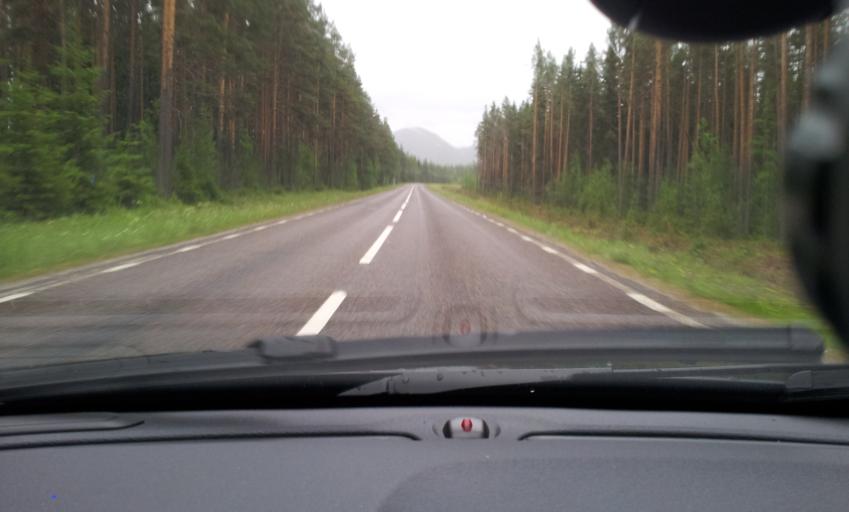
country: SE
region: Jaemtland
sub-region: Ragunda Kommun
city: Hammarstrand
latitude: 63.0814
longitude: 16.3685
